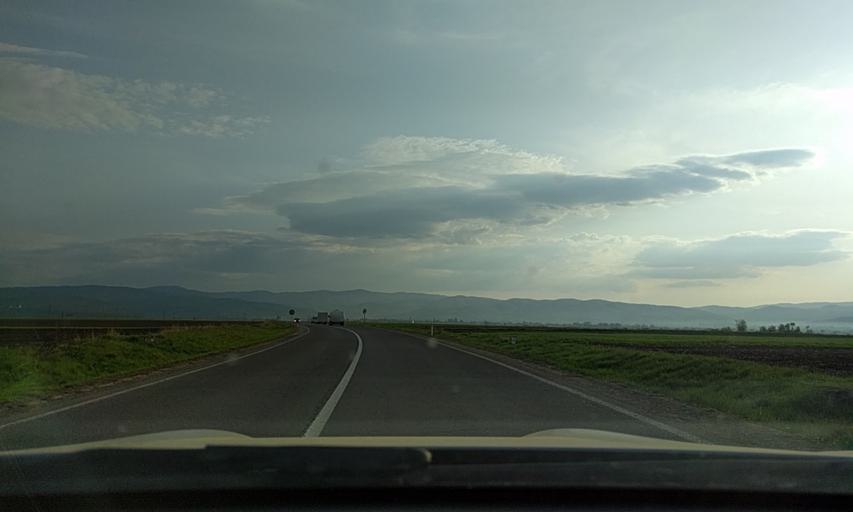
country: RO
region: Covasna
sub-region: Municipiul Targu Secuiesc
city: Lunga
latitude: 46.0319
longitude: 26.2377
